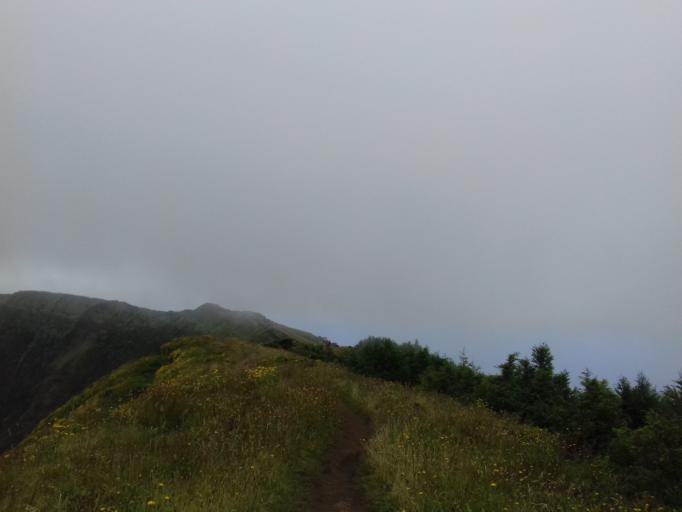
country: PT
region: Azores
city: Ribeira Grande
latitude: 38.5903
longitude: -28.7052
